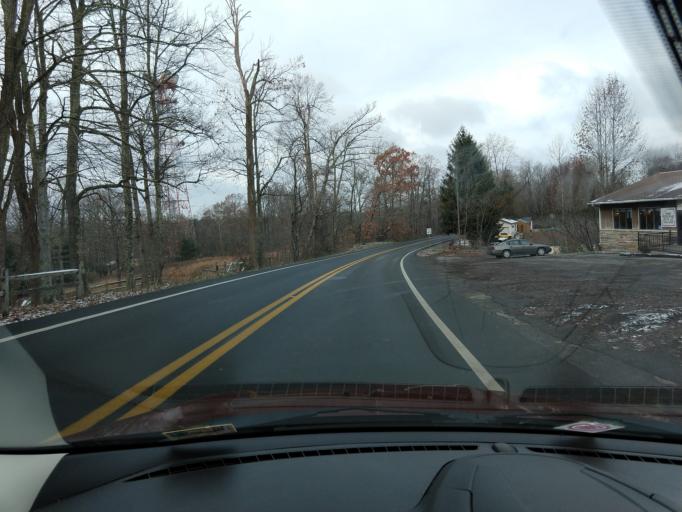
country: US
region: West Virginia
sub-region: Nicholas County
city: Craigsville
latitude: 38.2292
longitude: -80.6944
